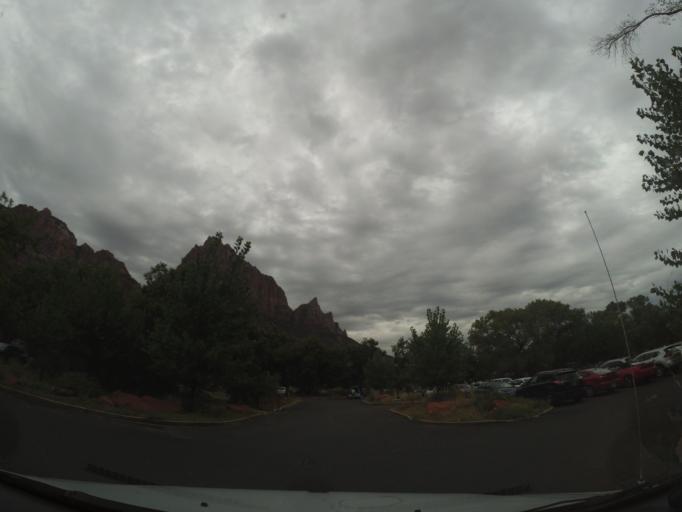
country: US
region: Utah
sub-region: Washington County
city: Hildale
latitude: 37.1988
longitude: -112.9873
